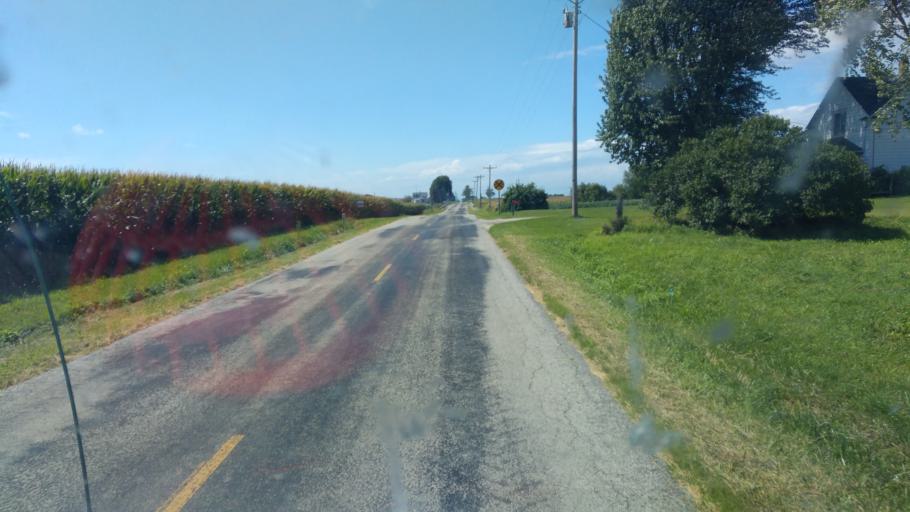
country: US
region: Ohio
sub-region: Marion County
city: Marion
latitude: 40.6587
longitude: -83.1882
